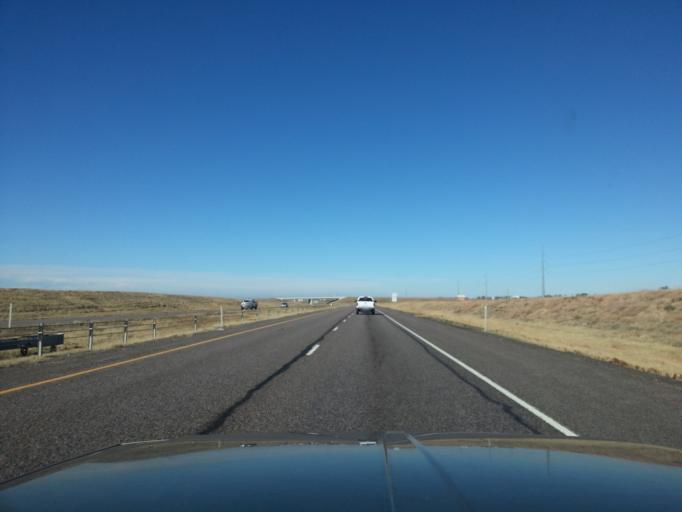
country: US
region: Colorado
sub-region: Adams County
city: Brighton
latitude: 39.8930
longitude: -104.7617
